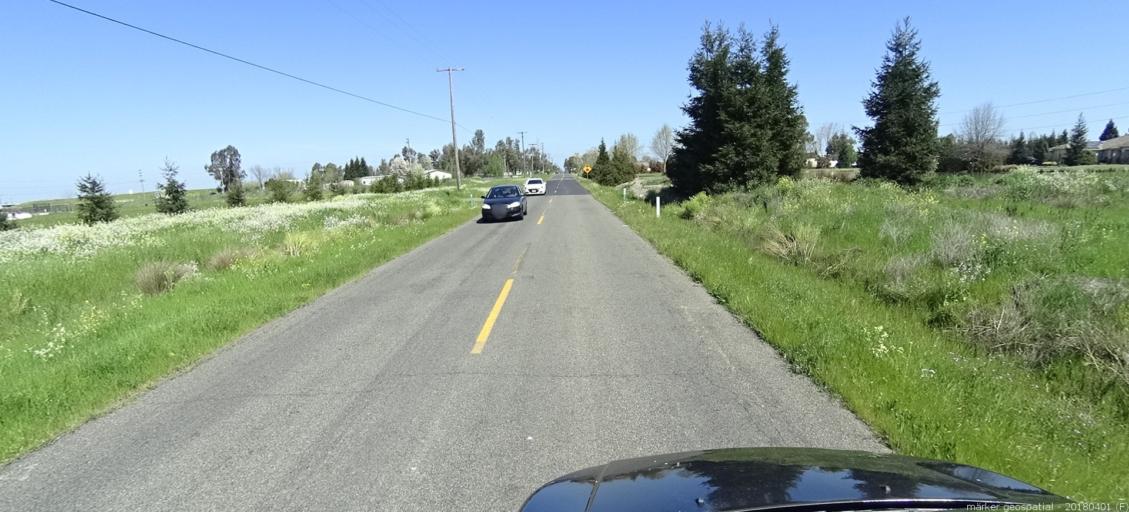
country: US
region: California
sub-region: Sacramento County
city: Herald
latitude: 38.3233
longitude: -121.2421
